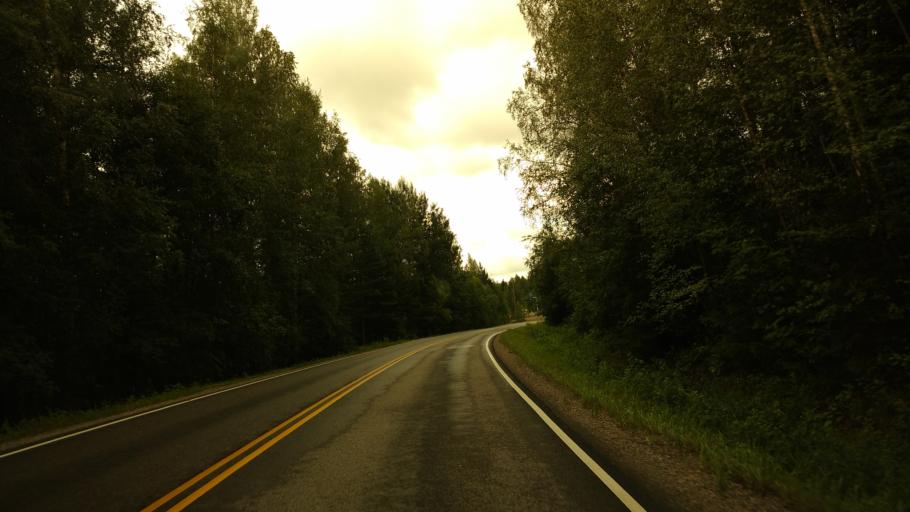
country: FI
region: Varsinais-Suomi
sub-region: Salo
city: Salo
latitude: 60.4409
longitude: 23.1823
